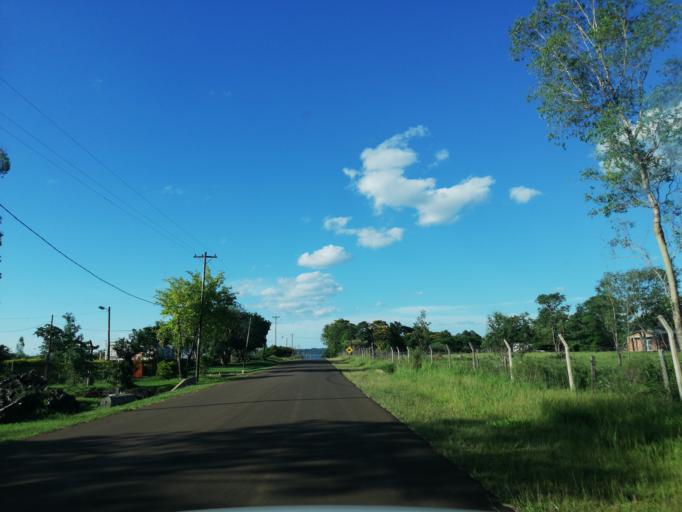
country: AR
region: Misiones
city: Garupa
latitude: -27.4616
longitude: -55.7971
